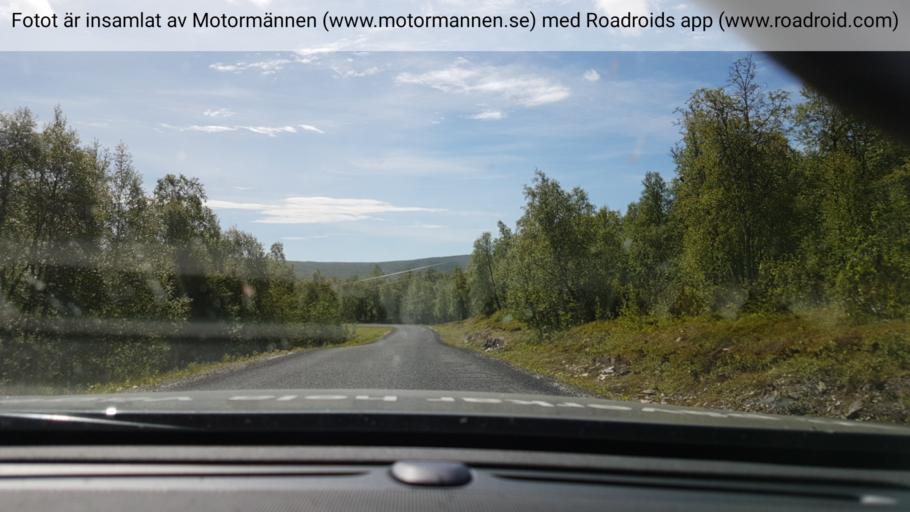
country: NO
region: Nordland
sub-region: Hattfjelldal
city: Hattfjelldal
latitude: 65.3431
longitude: 15.0996
